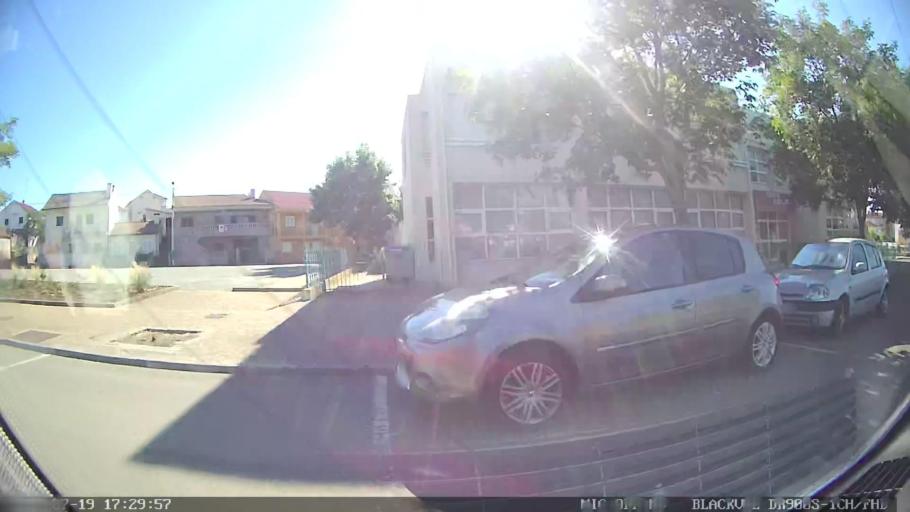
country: PT
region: Braganca
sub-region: Braganca Municipality
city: Braganca
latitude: 41.7959
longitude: -6.7709
